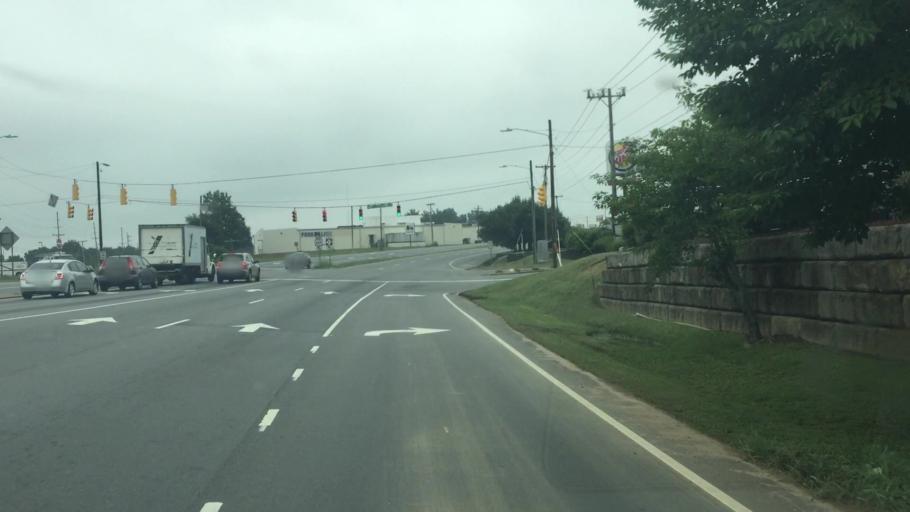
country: US
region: North Carolina
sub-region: Cabarrus County
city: Concord
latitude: 35.4005
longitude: -80.6087
